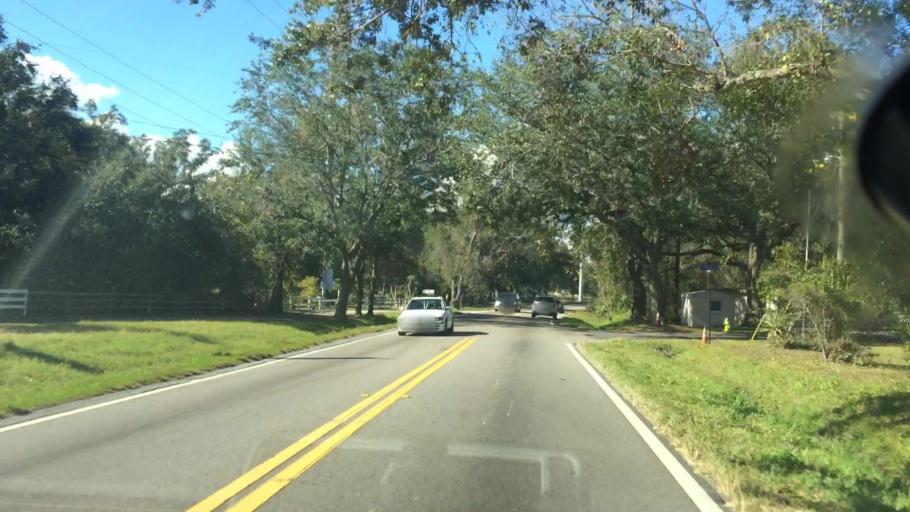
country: US
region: Florida
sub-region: Osceola County
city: Saint Cloud
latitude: 28.2614
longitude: -81.3419
